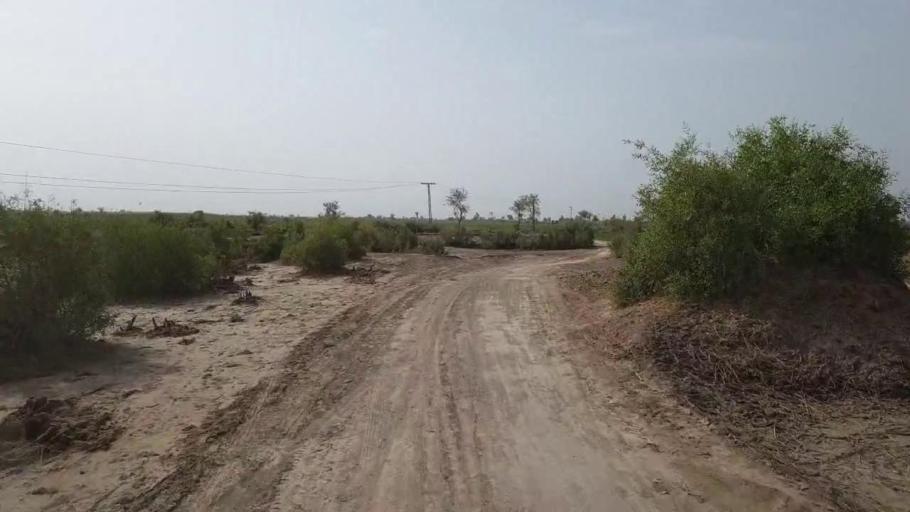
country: PK
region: Sindh
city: Daur
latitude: 26.4323
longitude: 68.1562
